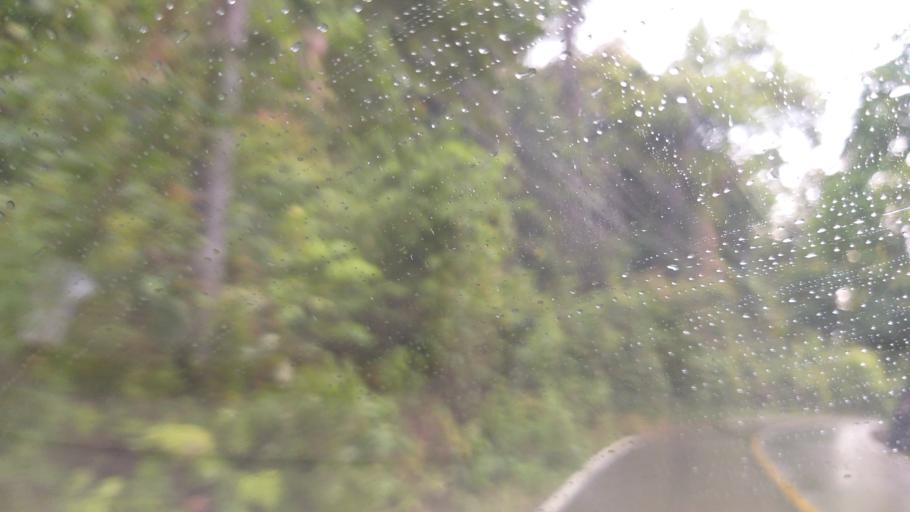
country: TH
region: Trat
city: Ko Chang Tai
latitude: 11.9754
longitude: 102.3196
